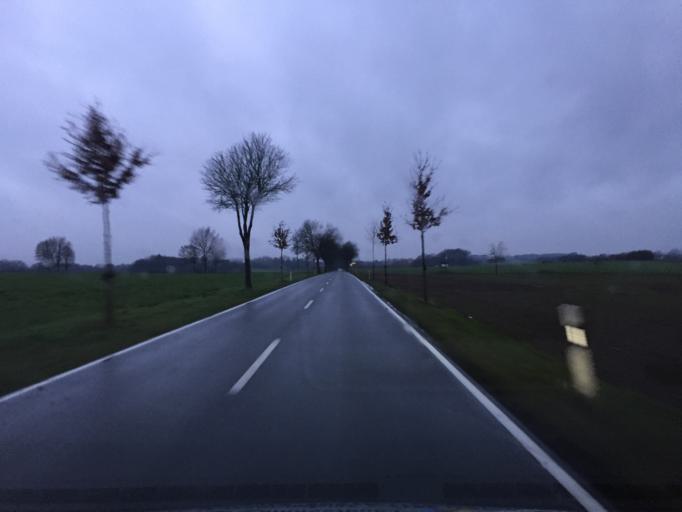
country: DE
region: Lower Saxony
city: Sustedt
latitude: 52.8905
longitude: 8.8908
